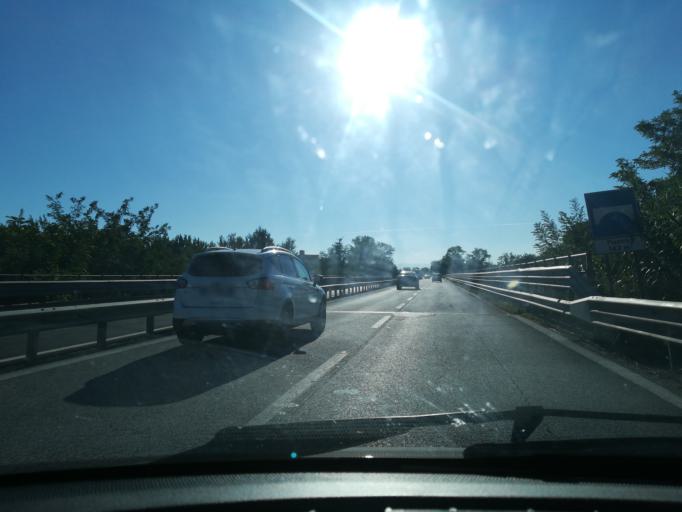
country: IT
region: The Marches
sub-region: Provincia di Macerata
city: Zona Industriale
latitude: 43.2632
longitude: 13.4777
